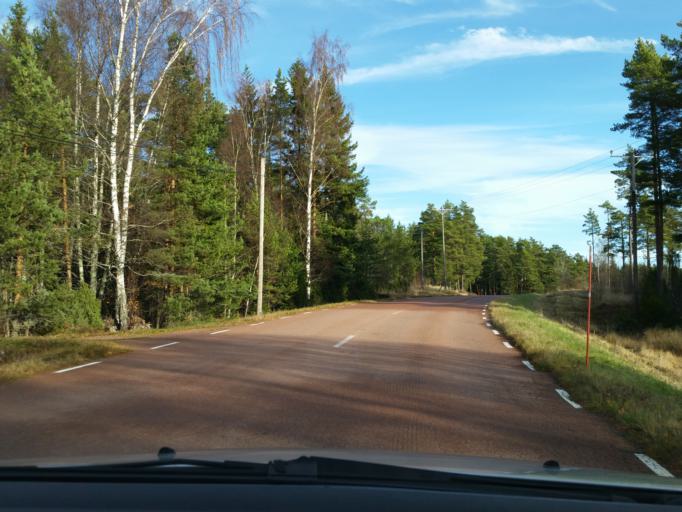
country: AX
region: Alands landsbygd
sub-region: Saltvik
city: Saltvik
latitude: 60.3231
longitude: 20.0799
